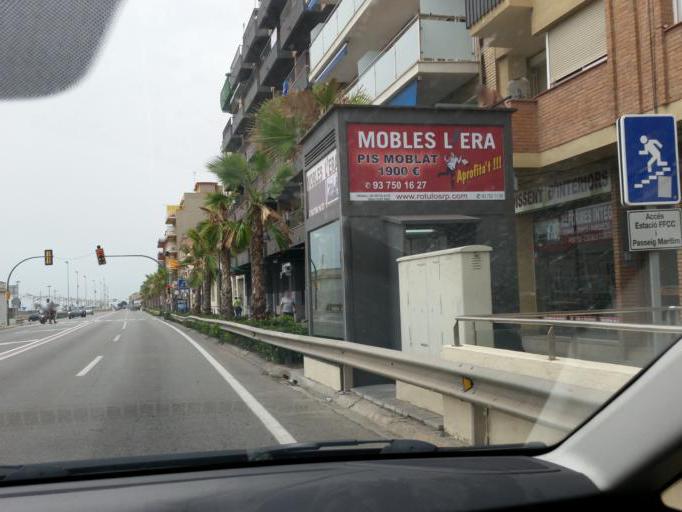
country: ES
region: Catalonia
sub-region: Provincia de Barcelona
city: Vilassar de Mar
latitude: 41.5010
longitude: 2.3902
